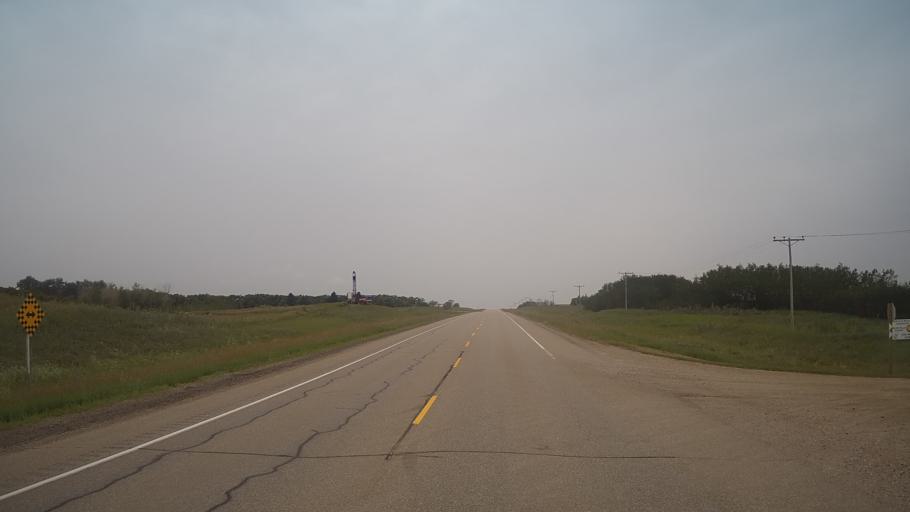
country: CA
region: Saskatchewan
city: Biggar
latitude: 52.0564
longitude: -107.8476
